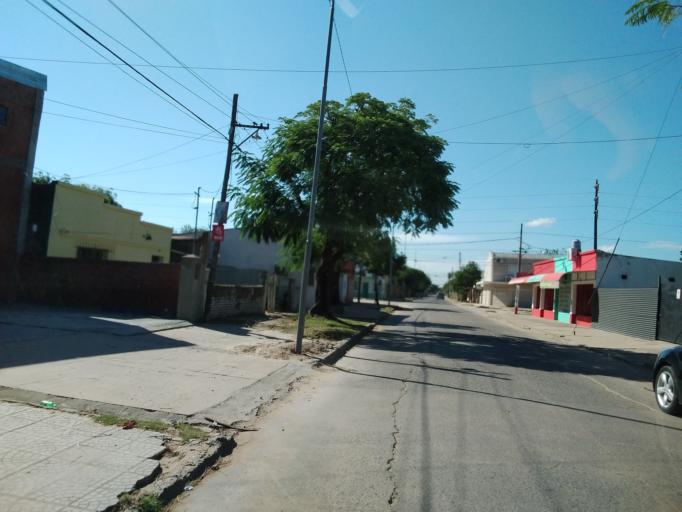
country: AR
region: Corrientes
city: Corrientes
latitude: -27.4819
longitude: -58.8067
